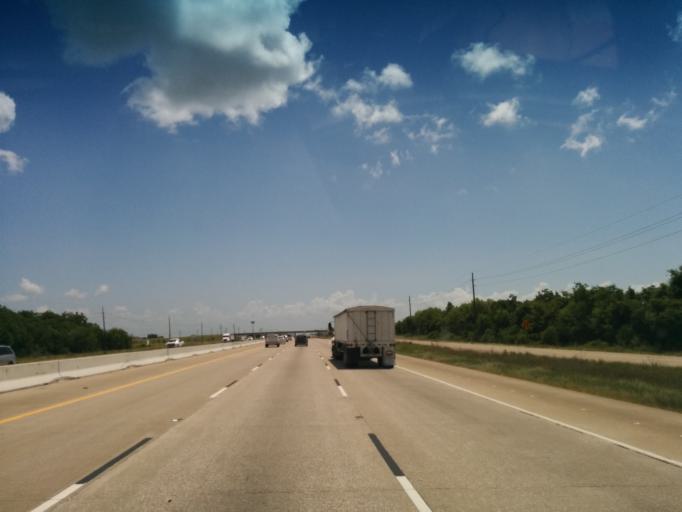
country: US
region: Texas
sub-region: Chambers County
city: Mont Belvieu
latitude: 29.8255
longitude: -94.8530
